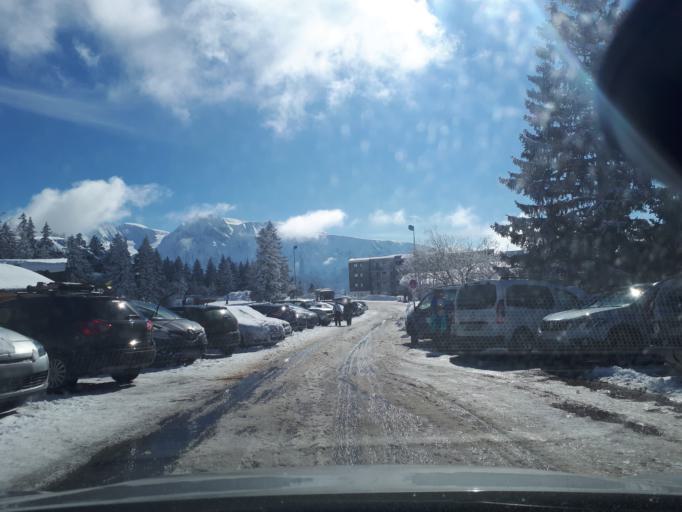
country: FR
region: Rhone-Alpes
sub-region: Departement de l'Isere
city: Vaulnaveys-le-Bas
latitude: 45.1062
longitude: 5.8754
